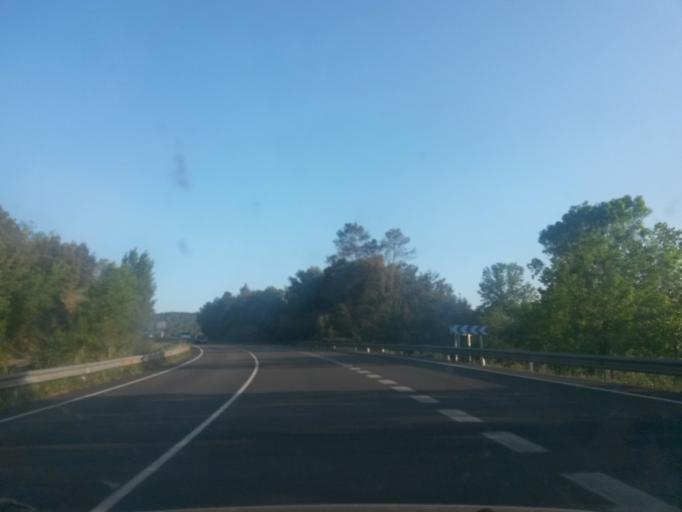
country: ES
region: Catalonia
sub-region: Provincia de Girona
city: Besalu
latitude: 42.1747
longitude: 2.7375
